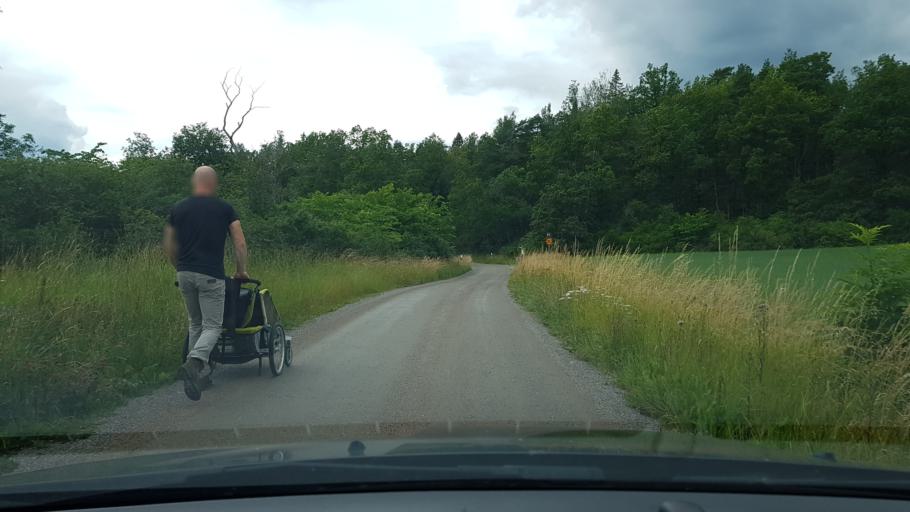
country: SE
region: Uppsala
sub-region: Uppsala Kommun
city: Alsike
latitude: 59.7198
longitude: 17.7001
